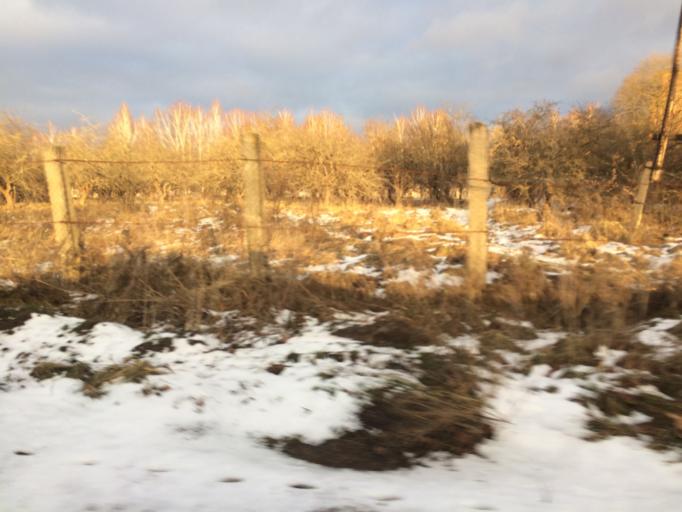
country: RU
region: Tula
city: Cherepet'
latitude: 54.1136
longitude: 36.3313
